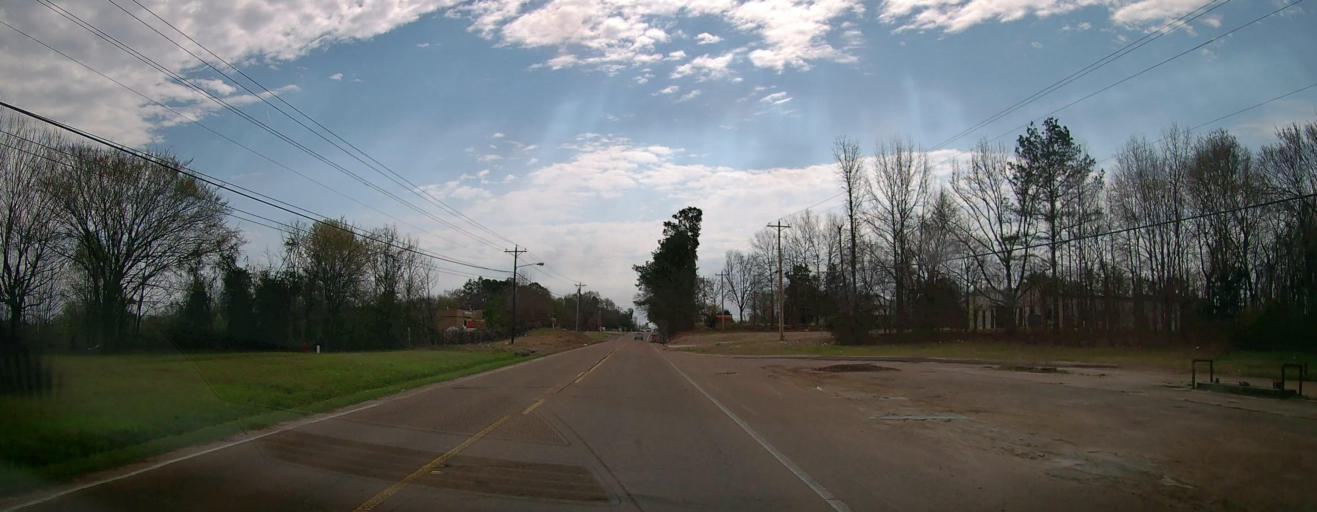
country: US
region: Mississippi
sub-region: De Soto County
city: Olive Branch
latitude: 34.9374
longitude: -89.8012
